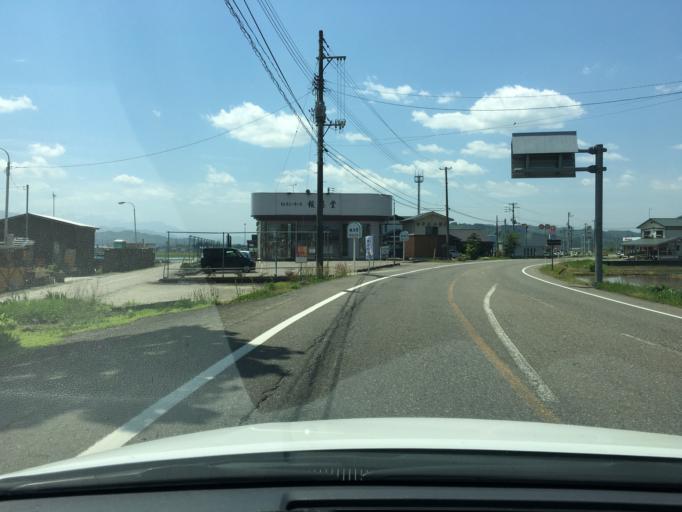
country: JP
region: Niigata
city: Ojiya
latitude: 37.2557
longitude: 138.9744
